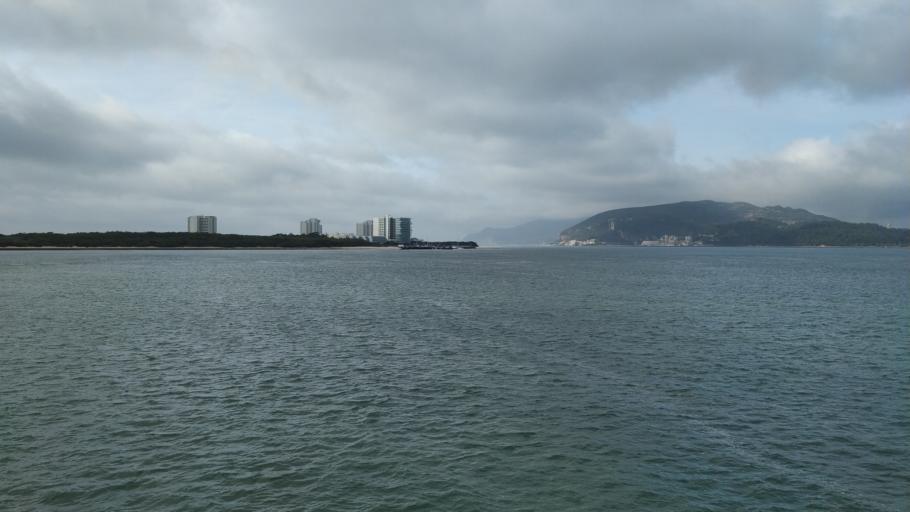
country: PT
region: Setubal
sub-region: Setubal
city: Setubal
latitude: 38.4996
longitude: -8.8887
